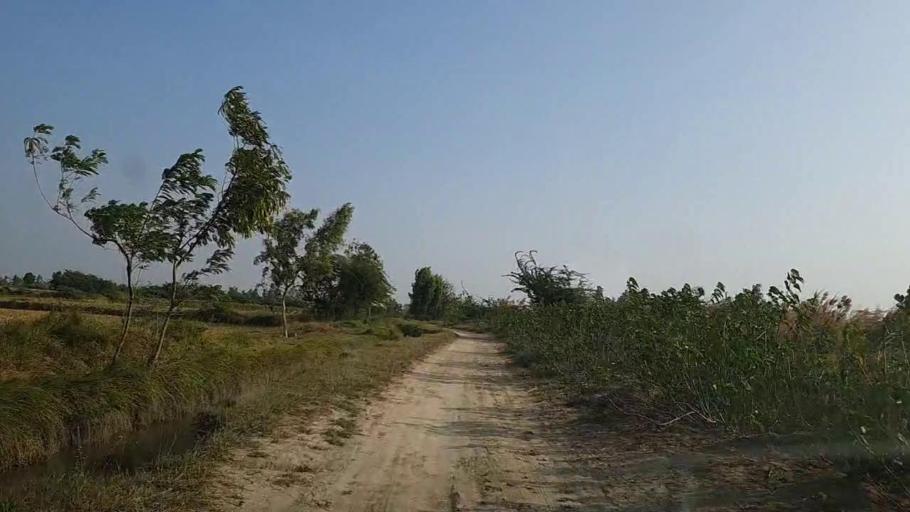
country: PK
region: Sindh
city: Mirpur Sakro
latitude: 24.5888
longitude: 67.6476
